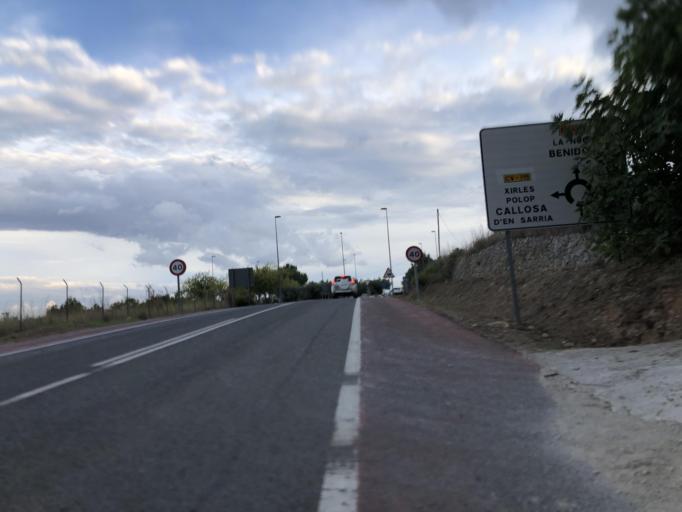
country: ES
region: Valencia
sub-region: Provincia de Alicante
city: Polop
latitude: 38.6311
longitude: -0.1489
